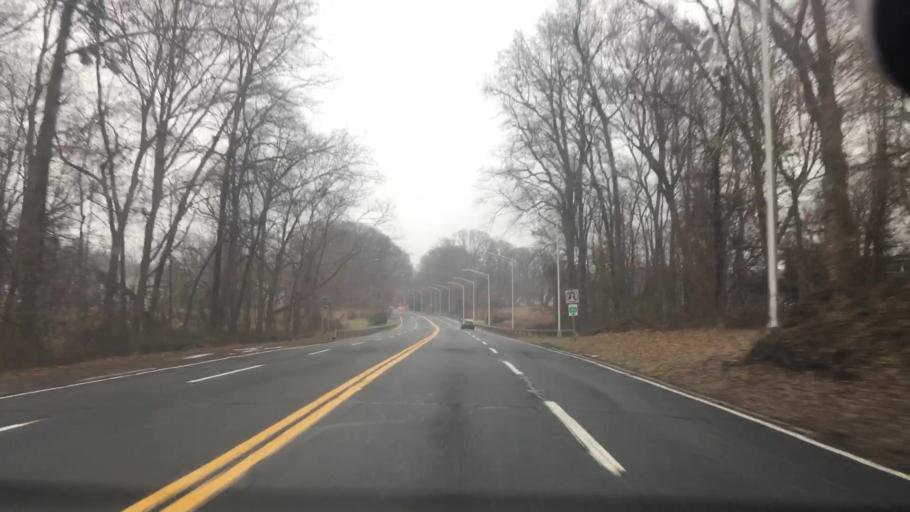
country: US
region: New York
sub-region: Westchester County
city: Rye
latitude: 40.9701
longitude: -73.6918
